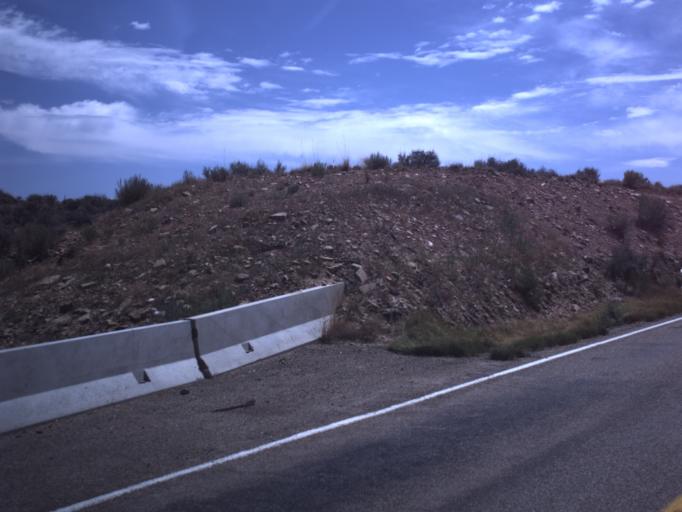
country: US
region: Utah
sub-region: Uintah County
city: Maeser
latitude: 40.3062
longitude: -109.6898
